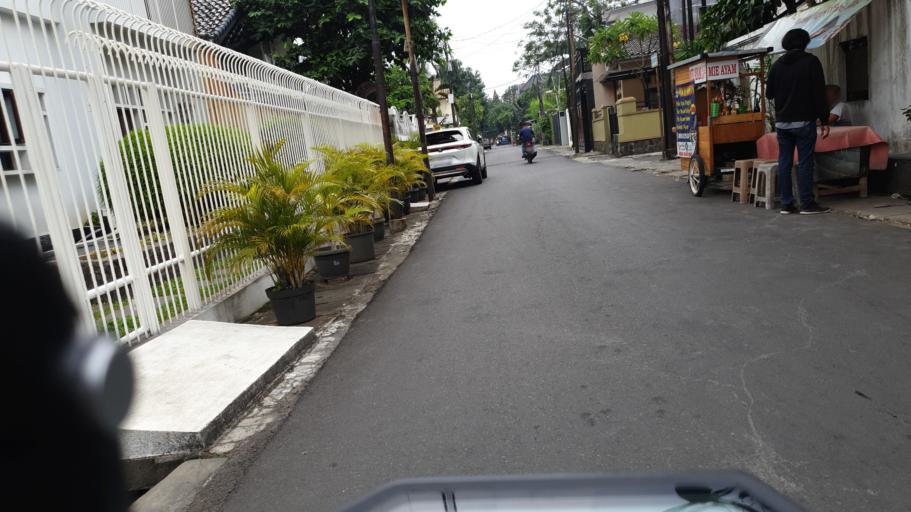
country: ID
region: Jakarta Raya
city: Jakarta
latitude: -6.2720
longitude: 106.7965
